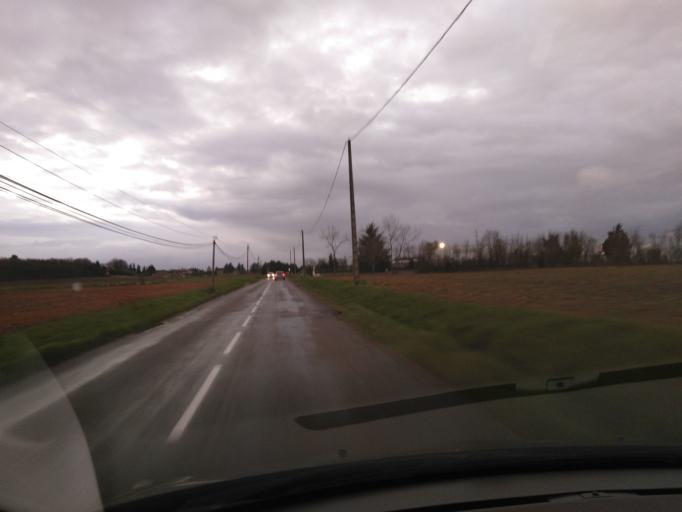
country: FR
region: Midi-Pyrenees
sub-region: Departement de la Haute-Garonne
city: Seilh
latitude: 43.6792
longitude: 1.3454
